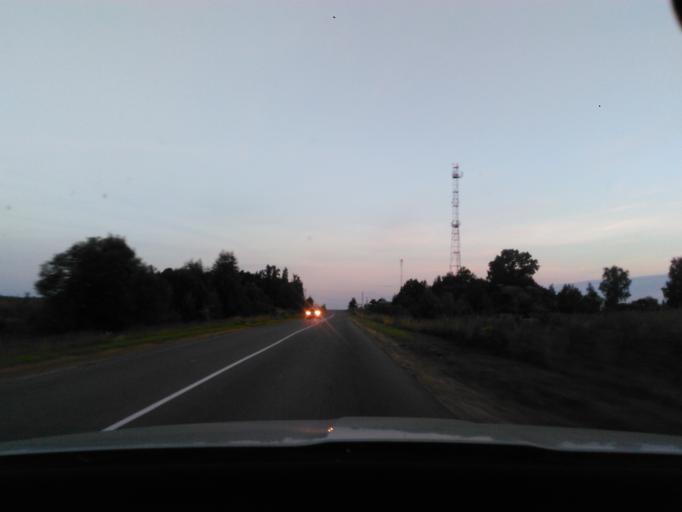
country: RU
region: Moskovskaya
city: Klin
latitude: 56.2350
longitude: 36.7505
